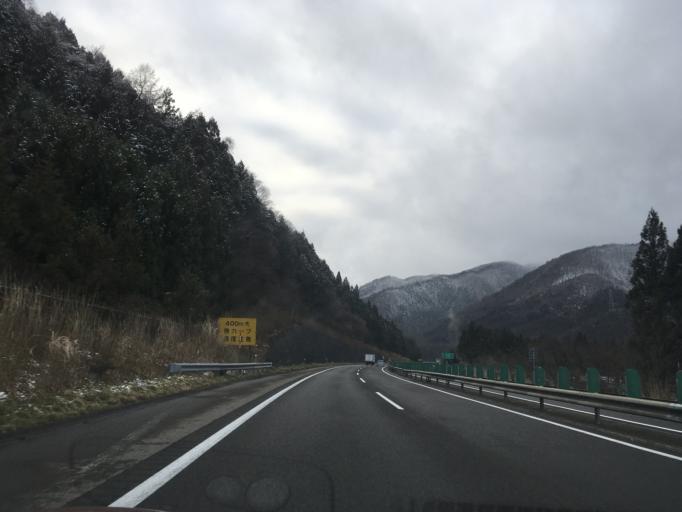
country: JP
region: Miyagi
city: Shiroishi
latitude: 38.2003
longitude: 140.5829
